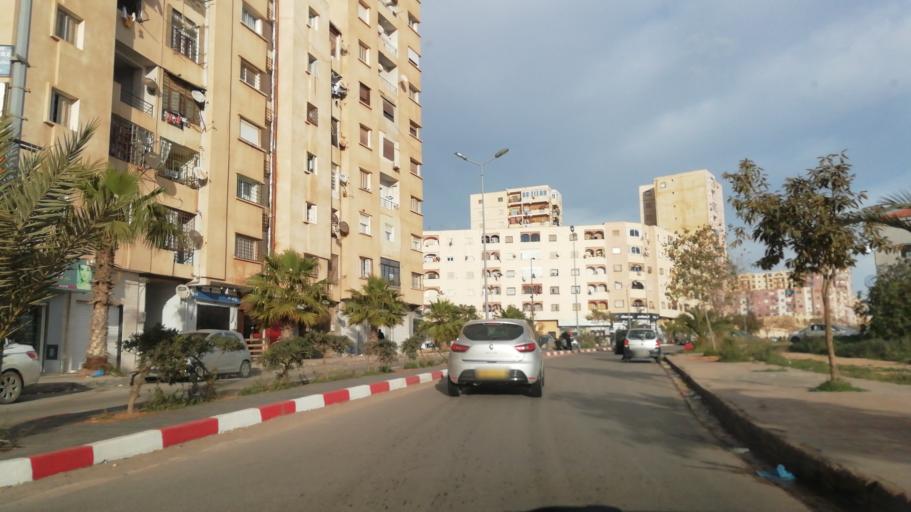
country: DZ
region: Oran
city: Bir el Djir
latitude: 35.7208
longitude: -0.5926
